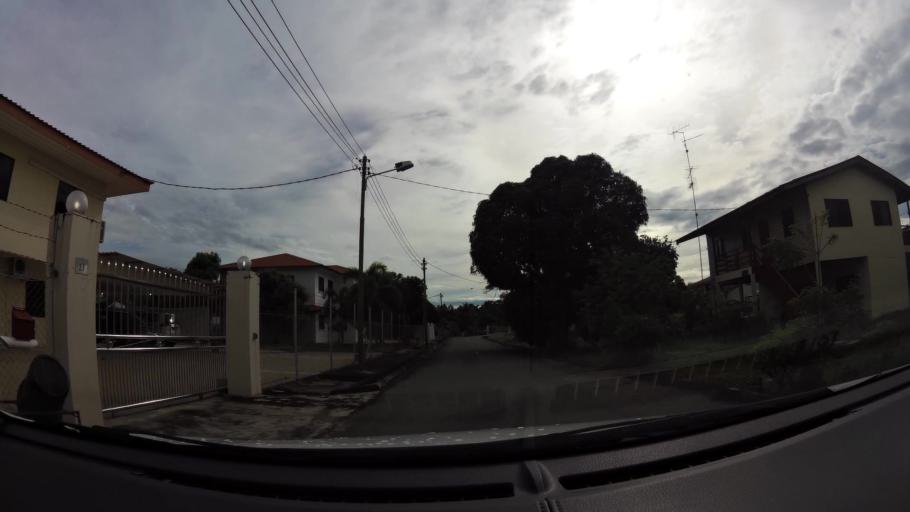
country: BN
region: Belait
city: Seria
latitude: 4.6157
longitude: 114.3620
